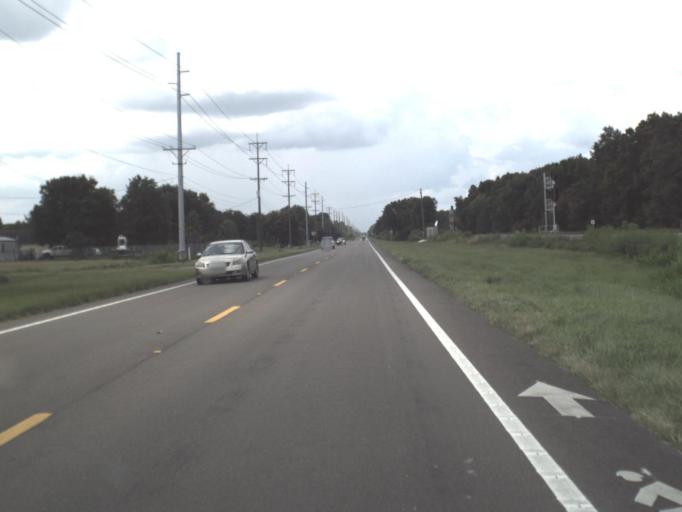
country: US
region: Florida
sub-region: Pasco County
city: Crystal Springs
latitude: 28.1322
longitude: -82.1485
